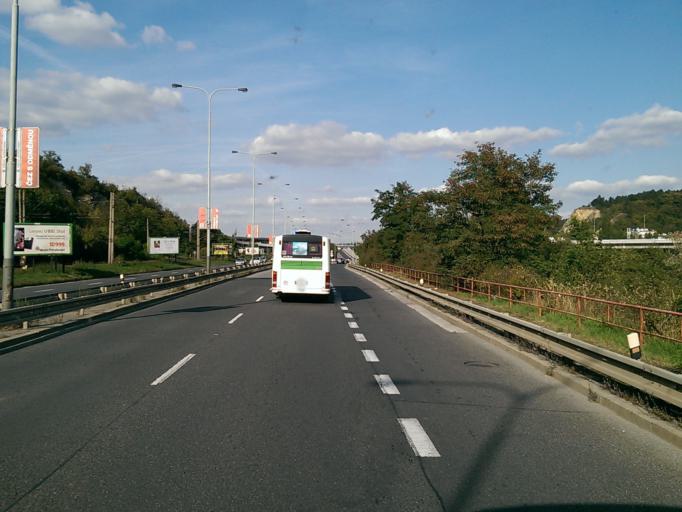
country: CZ
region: Praha
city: Branik
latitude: 50.0359
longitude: 14.4034
